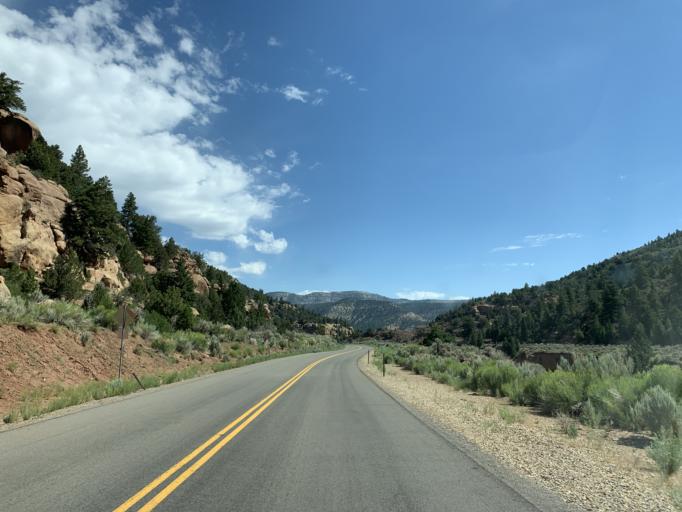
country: US
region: Utah
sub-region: Carbon County
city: East Carbon City
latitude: 39.7566
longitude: -110.5280
